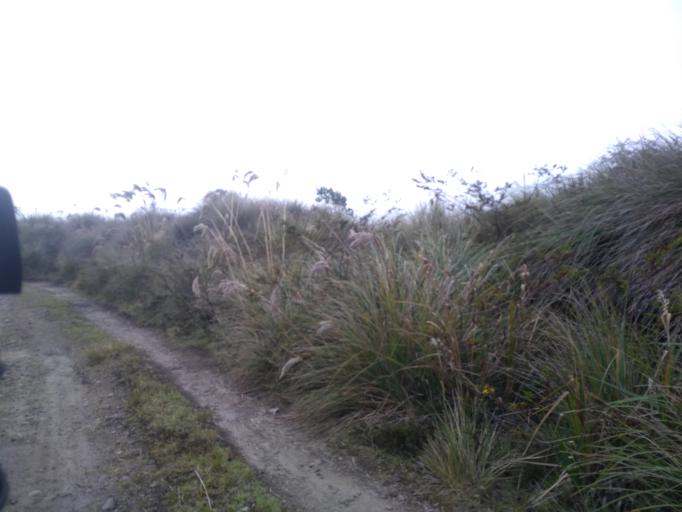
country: EC
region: Carchi
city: San Gabriel
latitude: 0.7079
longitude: -77.8259
